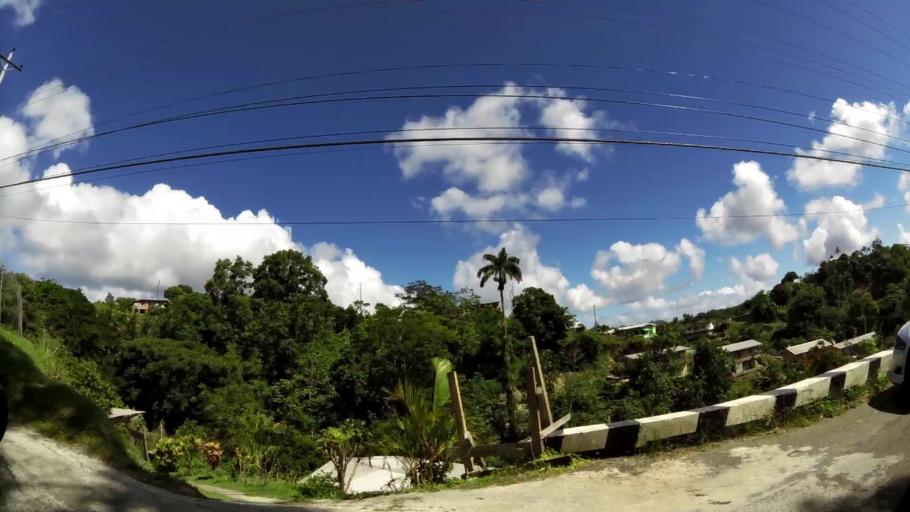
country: TT
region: Tobago
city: Scarborough
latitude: 11.2418
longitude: -60.7330
